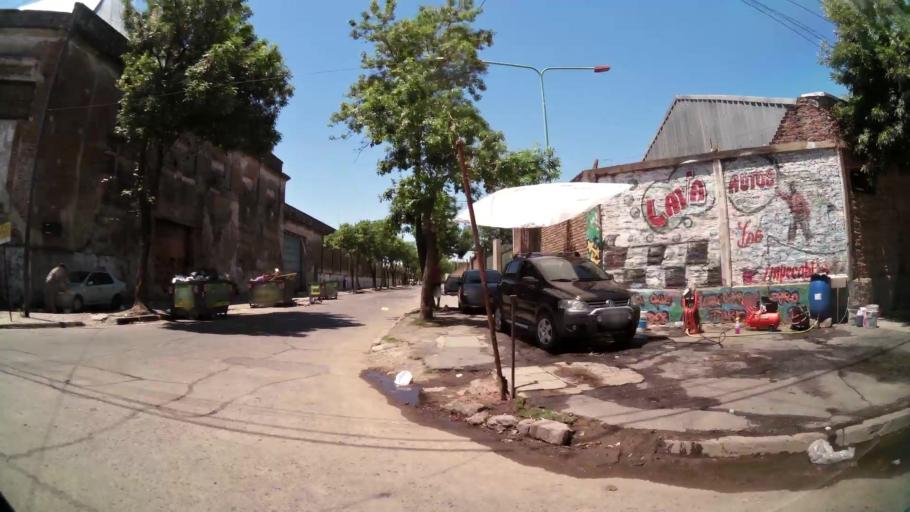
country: AR
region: Buenos Aires
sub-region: Partido de Avellaneda
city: Avellaneda
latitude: -34.6587
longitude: -58.3948
